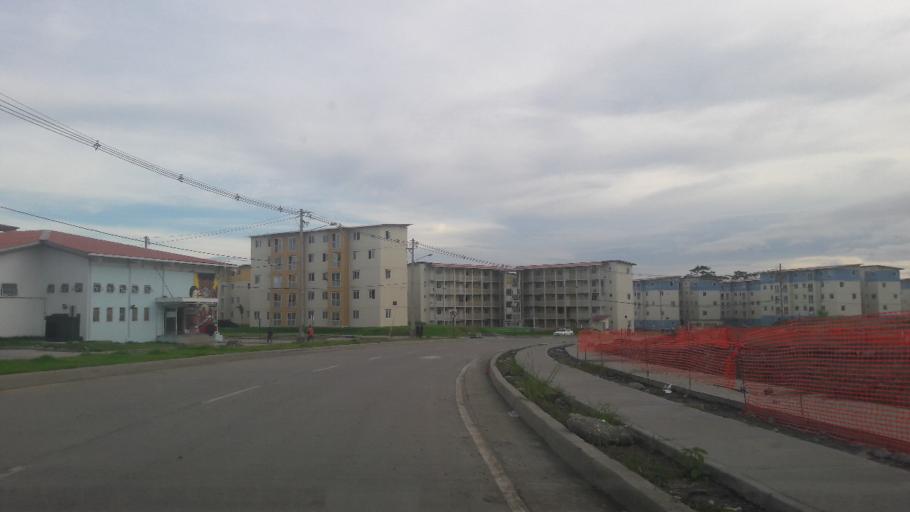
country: PA
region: Colon
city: Cativa
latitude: 9.3694
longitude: -79.8509
